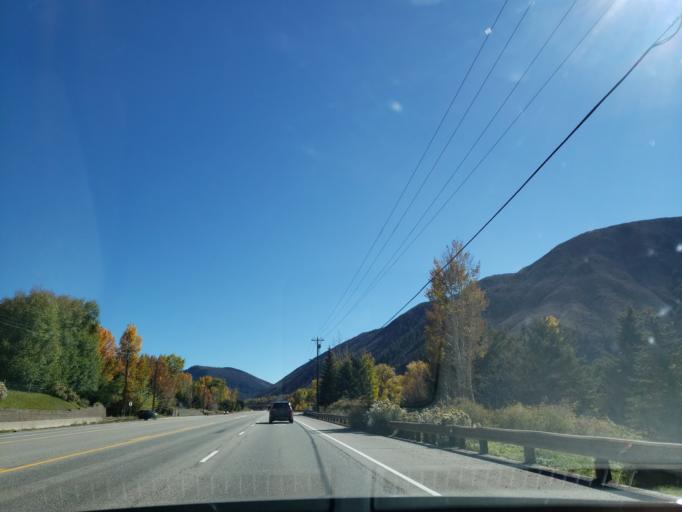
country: US
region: Colorado
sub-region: Eagle County
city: Basalt
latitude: 39.3514
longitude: -107.0177
